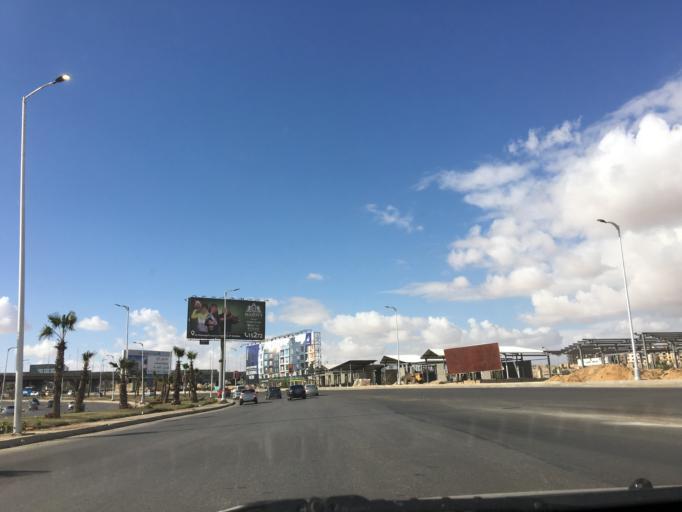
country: EG
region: Al Jizah
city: Awsim
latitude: 30.0094
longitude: 30.9852
